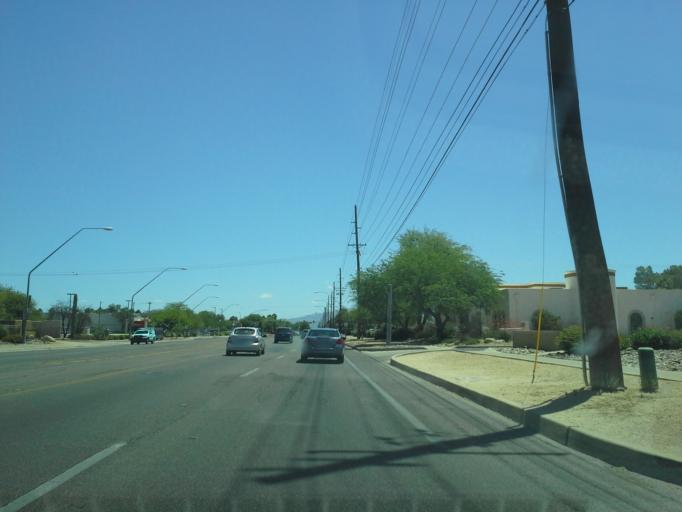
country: US
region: Arizona
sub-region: Pima County
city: Tucson
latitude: 32.2506
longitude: -110.8957
